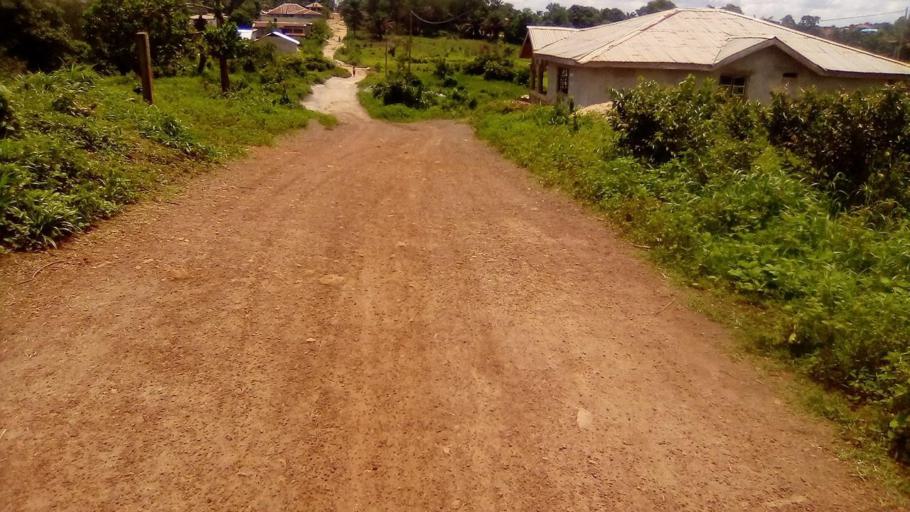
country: SL
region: Southern Province
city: Bo
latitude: 7.9356
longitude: -11.7452
